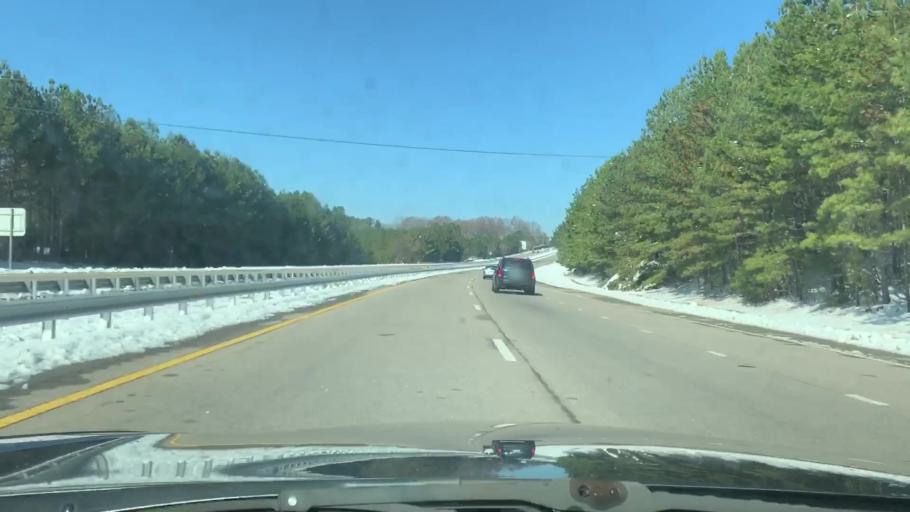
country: US
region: North Carolina
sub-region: Durham County
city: Durham
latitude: 36.0207
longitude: -78.9571
